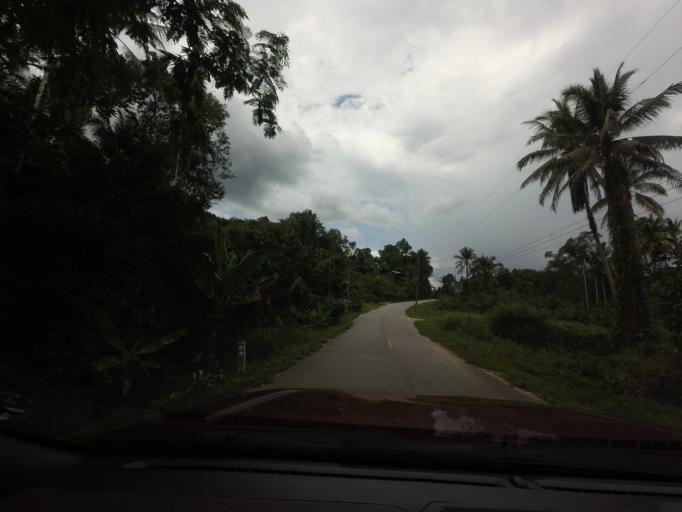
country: TH
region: Narathiwat
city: Sukhirin
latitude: 5.9845
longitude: 101.7059
